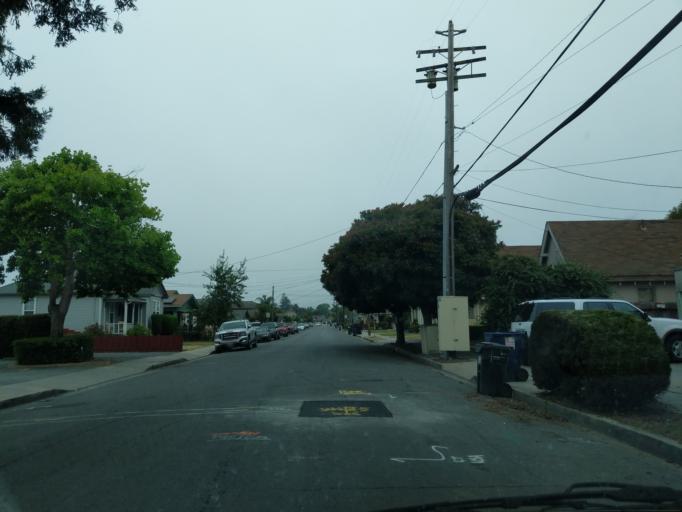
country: US
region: California
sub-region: Santa Cruz County
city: Watsonville
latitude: 36.9203
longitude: -121.7479
